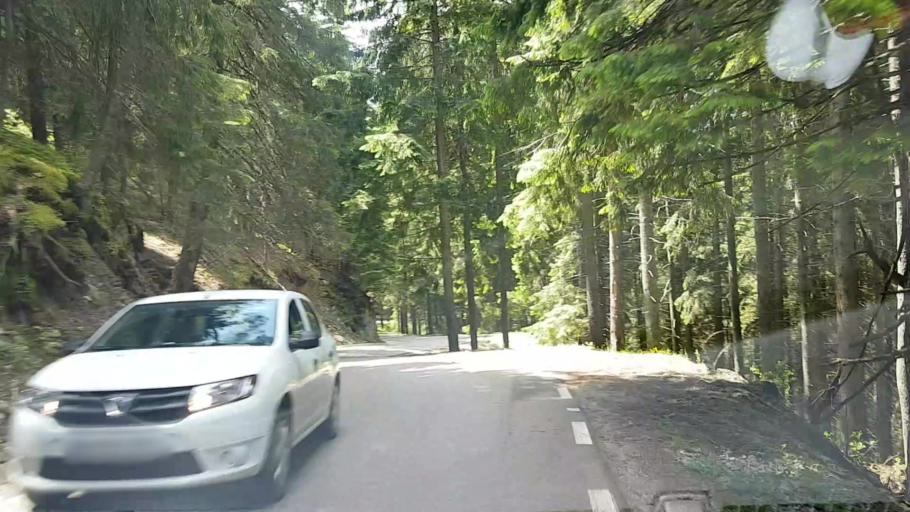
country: RO
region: Suceava
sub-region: Municipiul Campulung Moldovenesc
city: Campulung Moldovenesc
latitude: 47.4446
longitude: 25.5563
